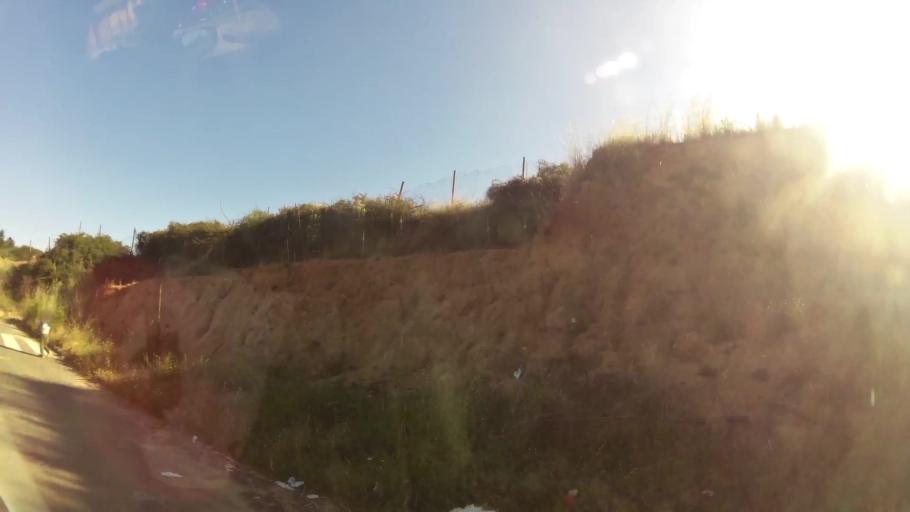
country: CL
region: Valparaiso
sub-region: Provincia de Valparaiso
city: Valparaiso
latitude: -33.1241
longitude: -71.5834
